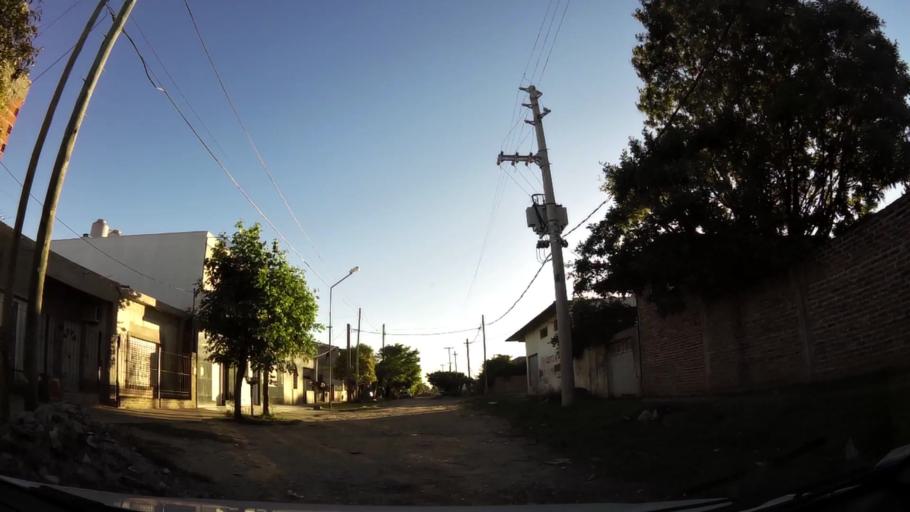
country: AR
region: Buenos Aires
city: San Justo
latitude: -34.7235
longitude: -58.6096
